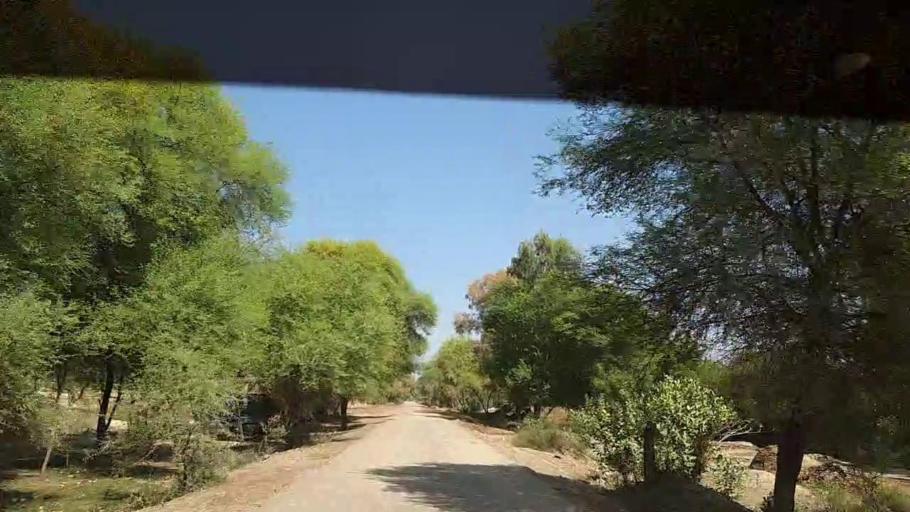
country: PK
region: Sindh
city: Tangwani
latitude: 28.2906
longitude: 69.0727
